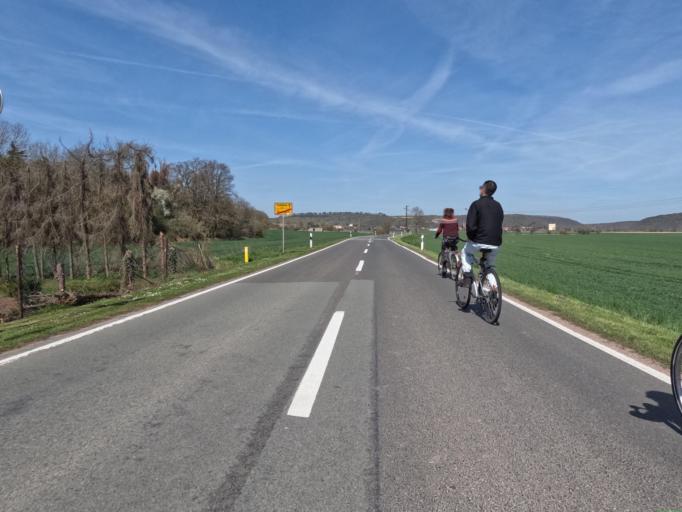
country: DE
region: Saxony-Anhalt
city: Beesenstedt
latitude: 51.6031
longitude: 11.7492
